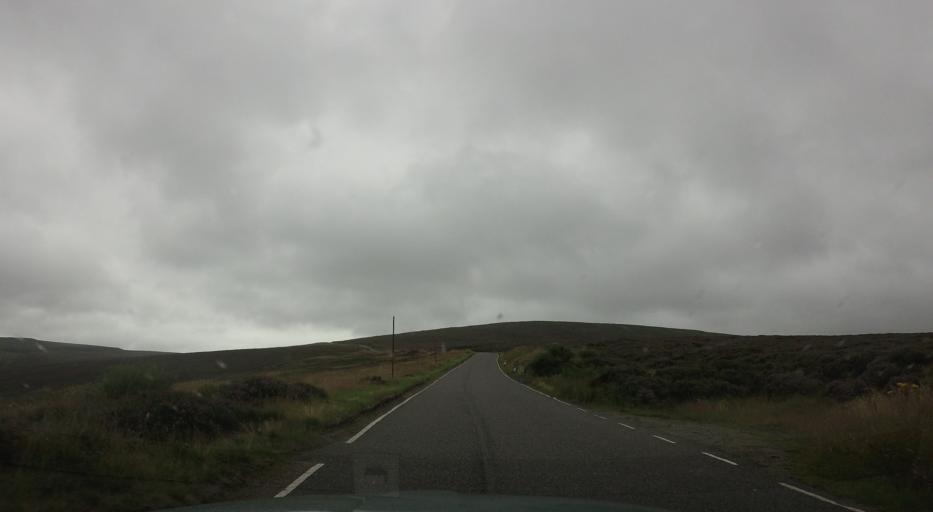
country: GB
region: Scotland
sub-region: Aberdeenshire
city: Banchory
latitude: 56.9405
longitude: -2.5747
